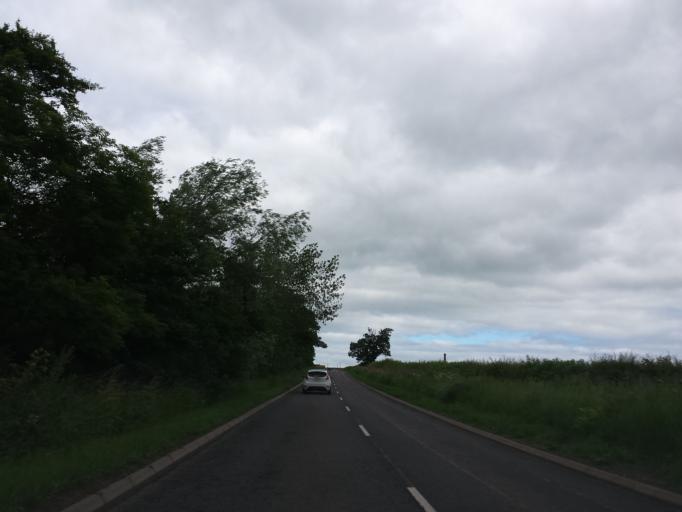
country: GB
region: Scotland
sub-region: East Lothian
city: Haddington
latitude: 55.9667
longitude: -2.7967
